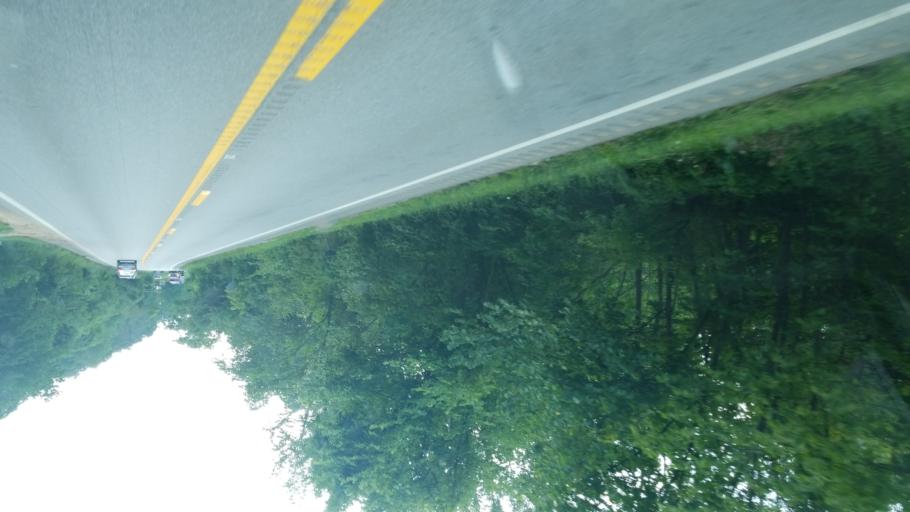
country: US
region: West Virginia
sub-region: Putnam County
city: Buffalo
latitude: 38.5988
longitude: -82.0055
